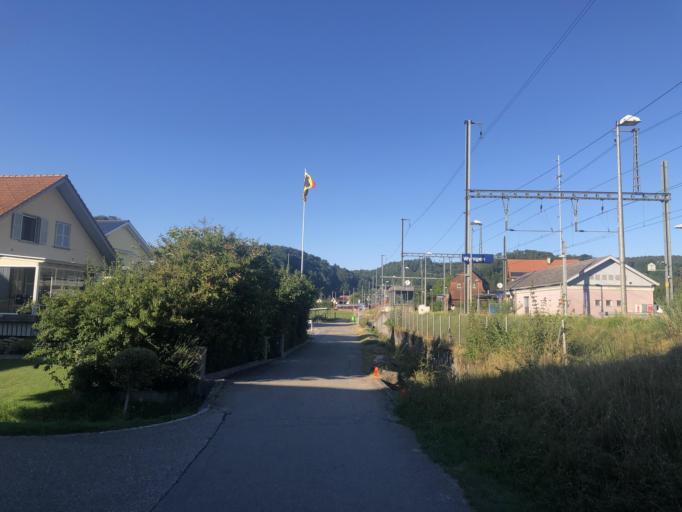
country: CH
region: Bern
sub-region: Emmental District
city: Wynigen
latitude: 47.1047
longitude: 7.6625
